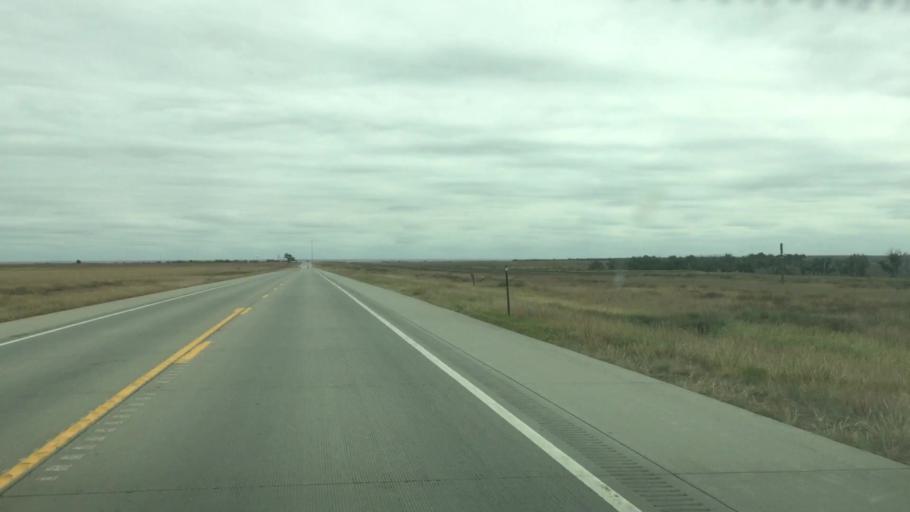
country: US
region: Colorado
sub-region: Kiowa County
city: Eads
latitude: 38.7657
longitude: -102.8446
